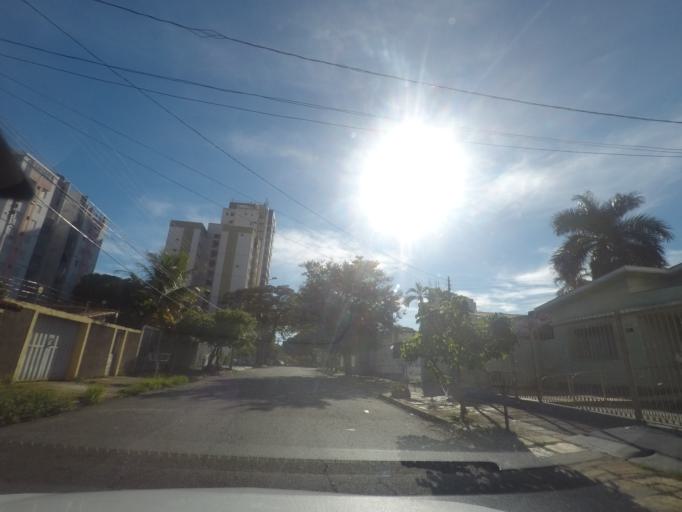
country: BR
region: Goias
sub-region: Goiania
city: Goiania
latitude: -16.6729
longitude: -49.2739
